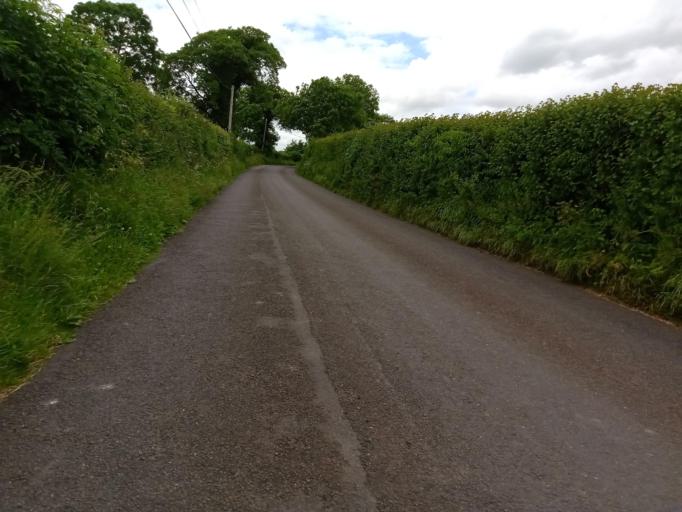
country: IE
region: Leinster
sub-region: Kilkenny
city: Kilkenny
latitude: 52.6893
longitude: -7.2496
